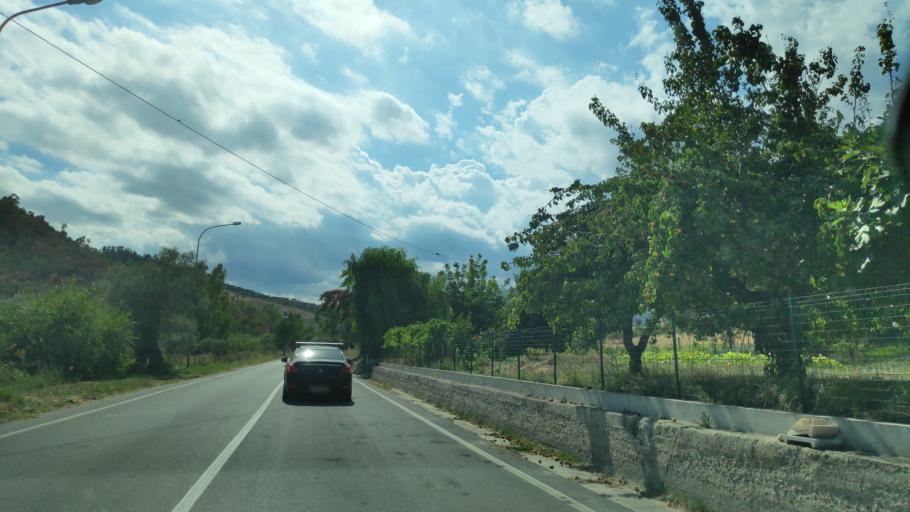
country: IT
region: Calabria
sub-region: Provincia di Catanzaro
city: Santa Caterina dello Ionio Marina
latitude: 38.5276
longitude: 16.5637
